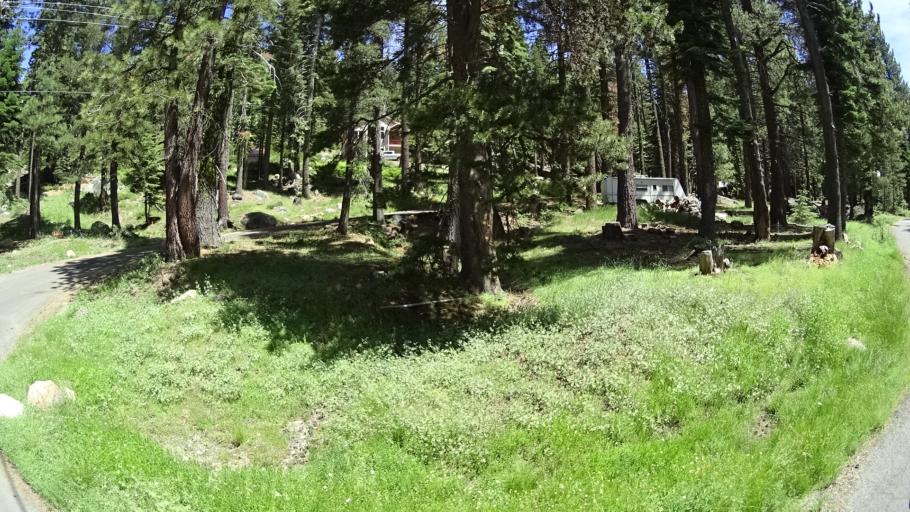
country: US
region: California
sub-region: Calaveras County
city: Arnold
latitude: 38.4234
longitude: -120.1013
